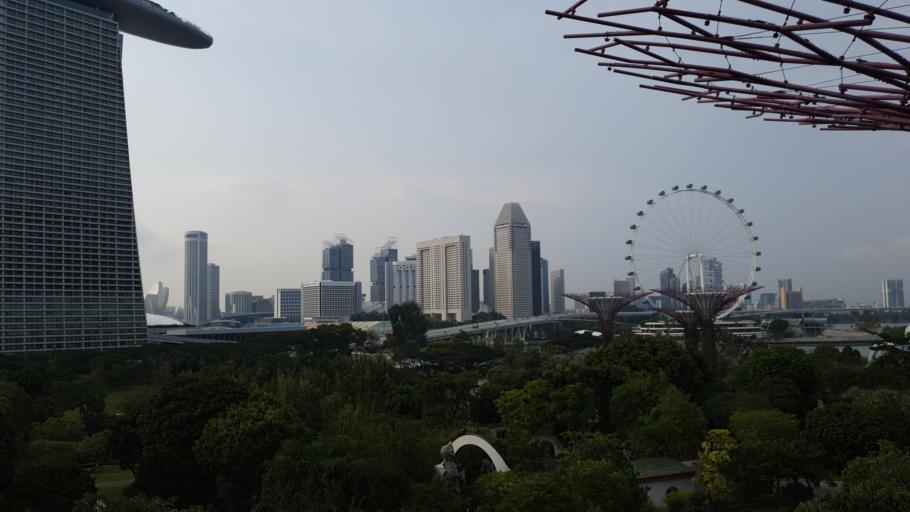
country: SG
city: Singapore
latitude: 1.2823
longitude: 103.8638
